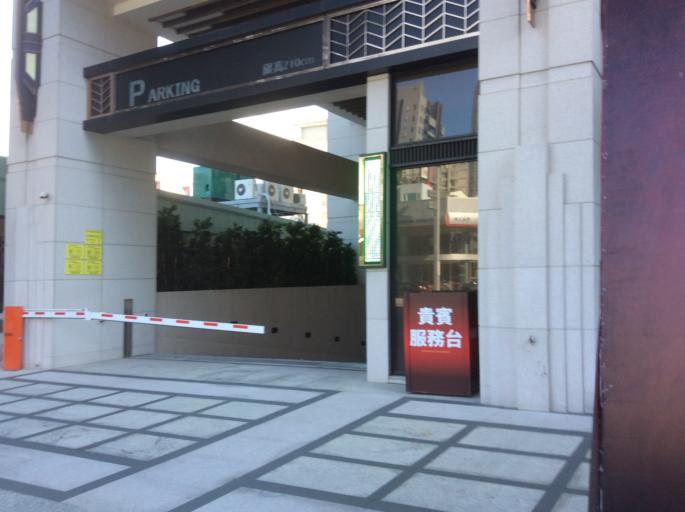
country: TW
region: Kaohsiung
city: Kaohsiung
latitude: 22.6818
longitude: 120.3110
